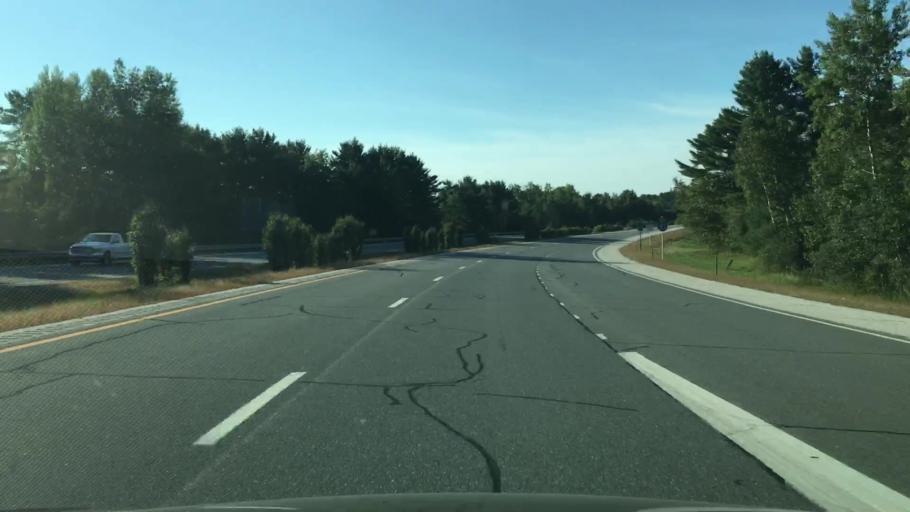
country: US
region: New Hampshire
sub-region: Grafton County
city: Littleton
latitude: 44.2303
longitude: -71.7510
